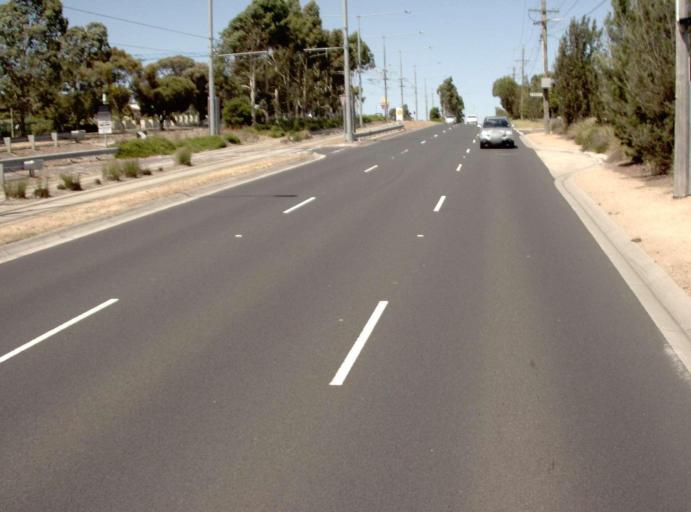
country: AU
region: Victoria
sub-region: Whitehorse
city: Vermont South
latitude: -37.8559
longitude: 145.1768
